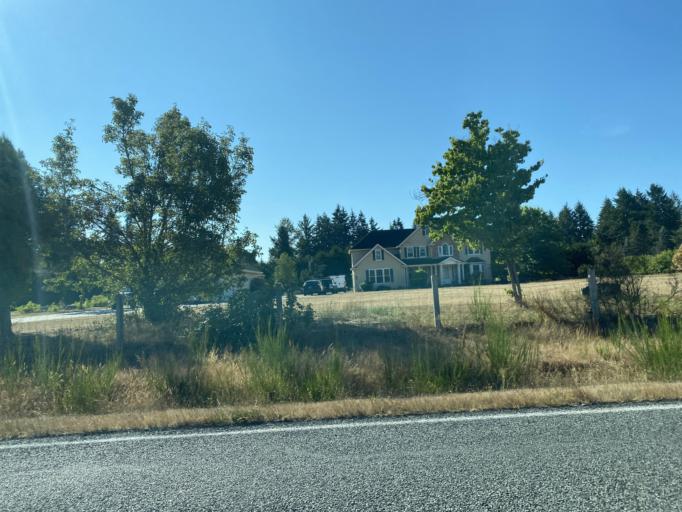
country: US
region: Washington
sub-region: Thurston County
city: Tanglewilde-Thompson Place
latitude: 47.0115
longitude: -122.7321
